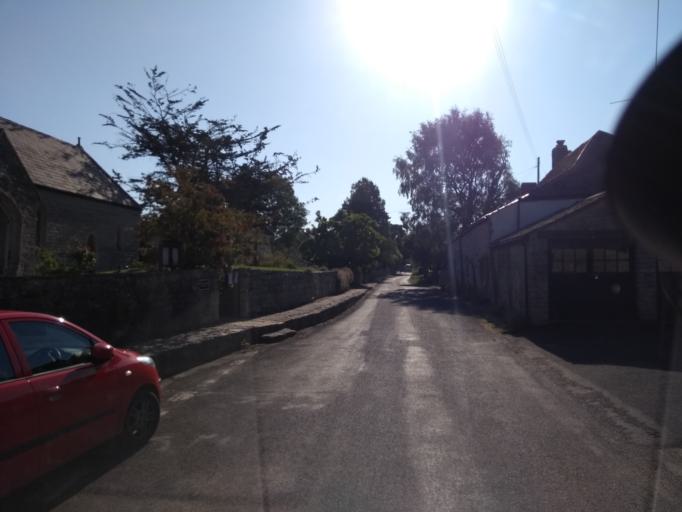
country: GB
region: England
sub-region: Somerset
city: Westonzoyland
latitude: 51.1402
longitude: -2.9049
